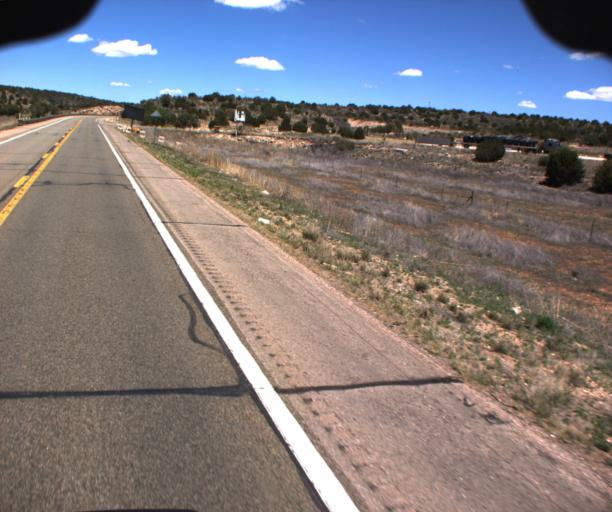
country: US
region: Arizona
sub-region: Yavapai County
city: Paulden
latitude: 34.9209
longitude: -112.4536
